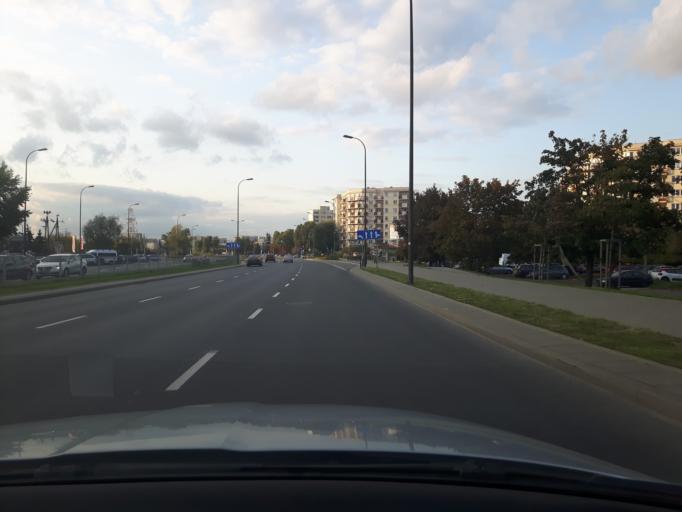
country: PL
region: Masovian Voivodeship
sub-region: Warszawa
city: Ursynow
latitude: 52.1463
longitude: 21.0372
